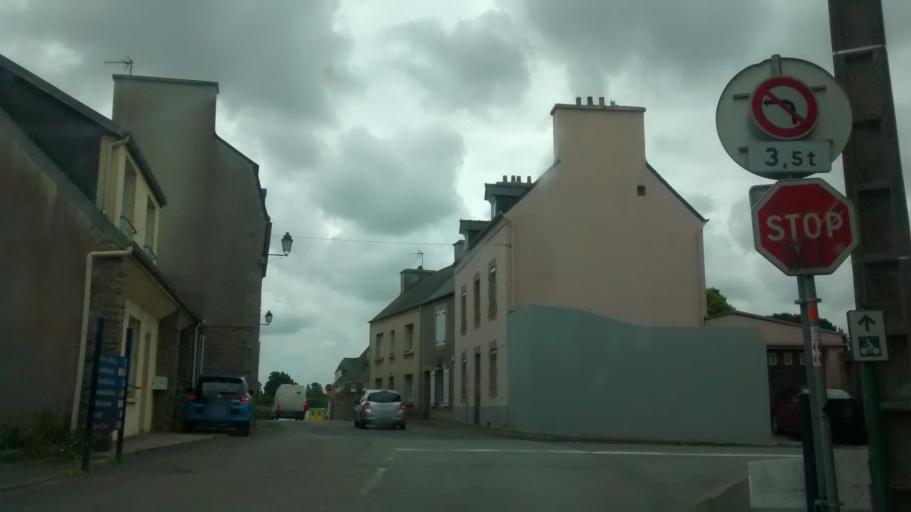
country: FR
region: Brittany
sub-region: Departement du Finistere
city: Guisseny
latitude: 48.6348
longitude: -4.4108
